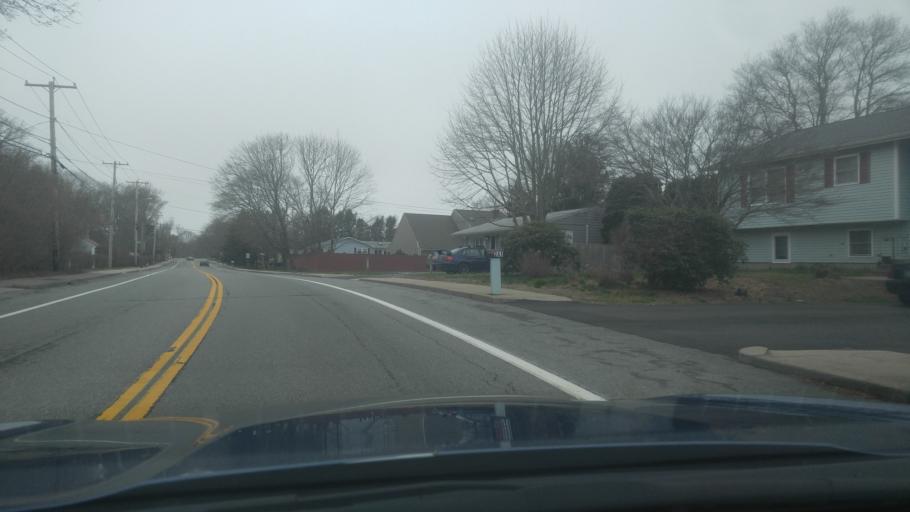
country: US
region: Rhode Island
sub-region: Washington County
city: Narragansett Pier
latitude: 41.4347
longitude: -71.4727
